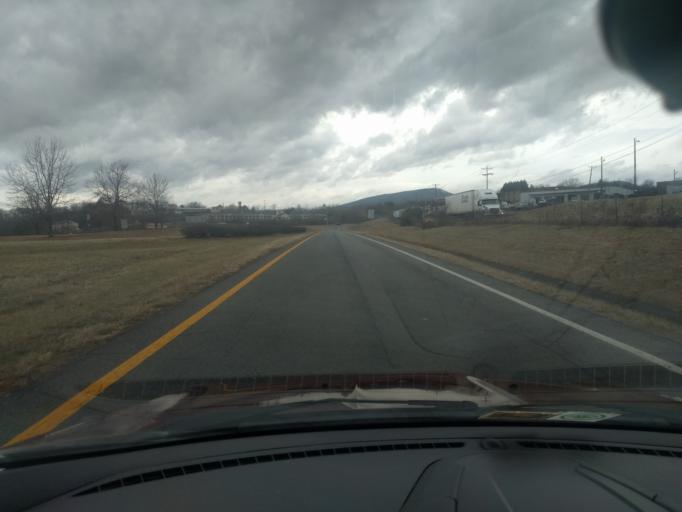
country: US
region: Virginia
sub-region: Roanoke County
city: Hollins
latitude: 37.3291
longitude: -79.9871
